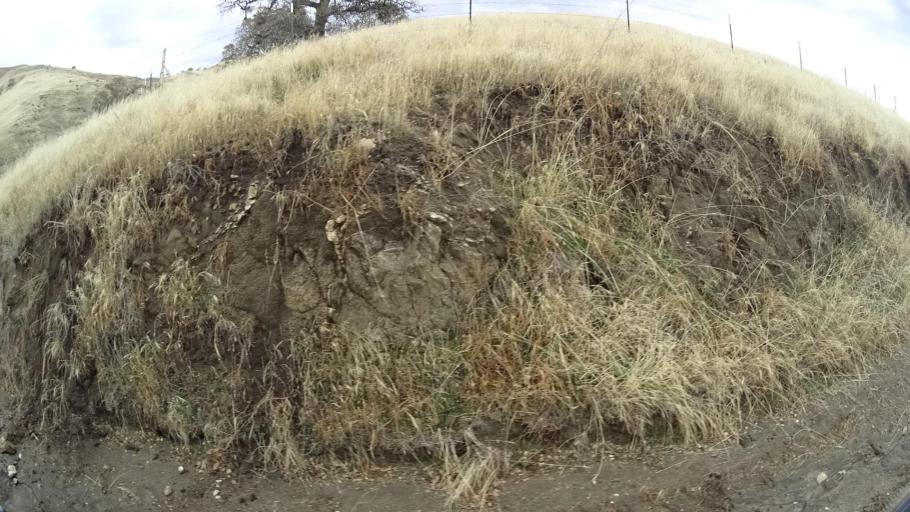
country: US
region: California
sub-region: Kern County
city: Arvin
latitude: 35.1258
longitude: -118.7546
